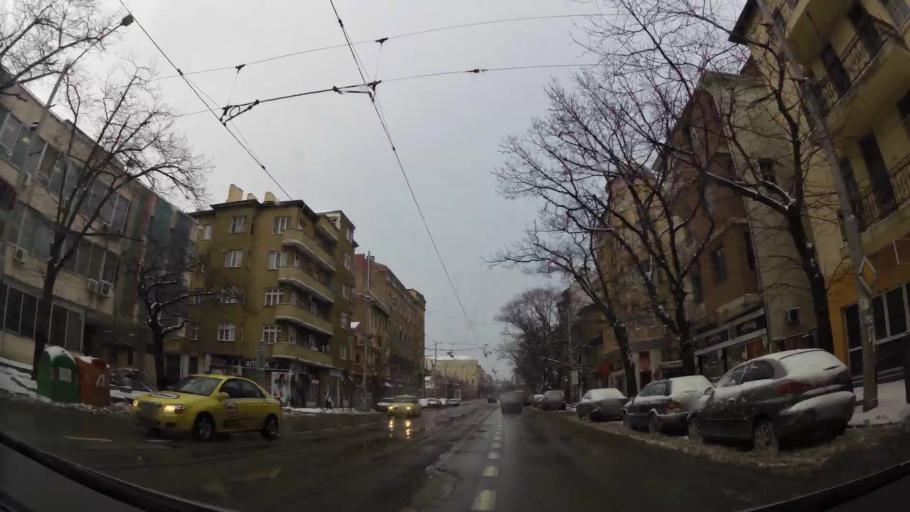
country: BG
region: Sofia-Capital
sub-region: Stolichna Obshtina
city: Sofia
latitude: 42.6982
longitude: 23.3122
